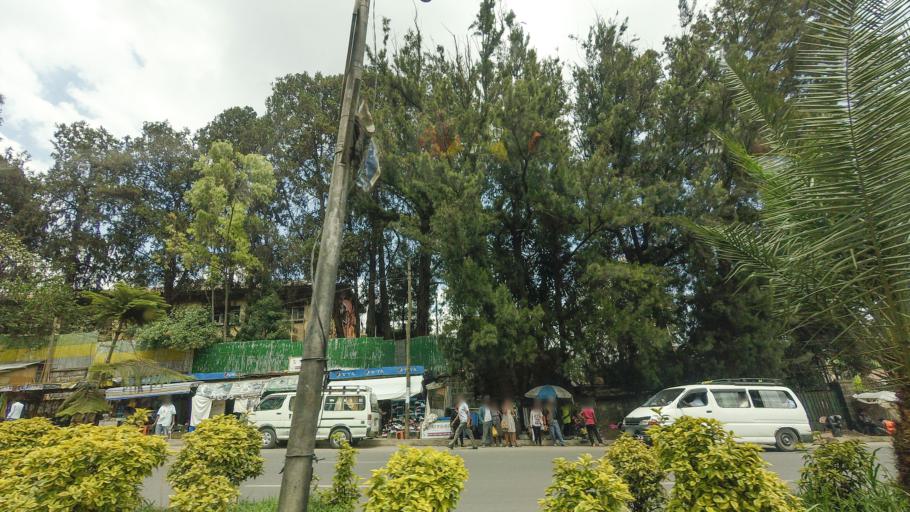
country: ET
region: Adis Abeba
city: Addis Ababa
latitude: 9.0217
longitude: 38.7522
